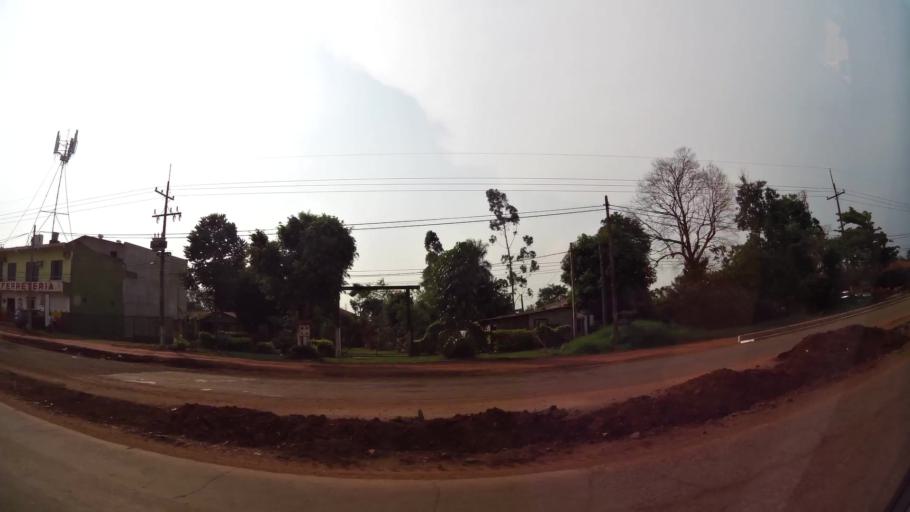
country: PY
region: Alto Parana
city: Ciudad del Este
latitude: -25.4735
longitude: -54.6484
